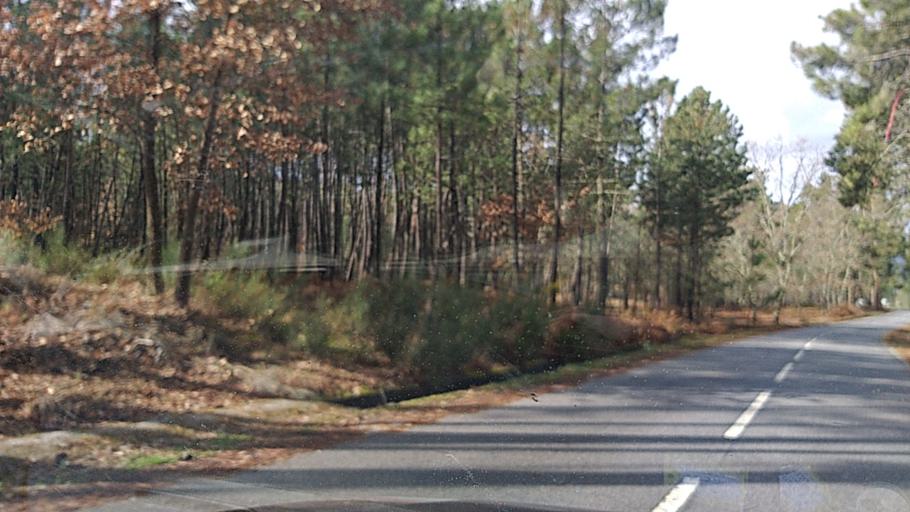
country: PT
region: Guarda
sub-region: Fornos de Algodres
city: Fornos de Algodres
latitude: 40.6619
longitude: -7.6409
